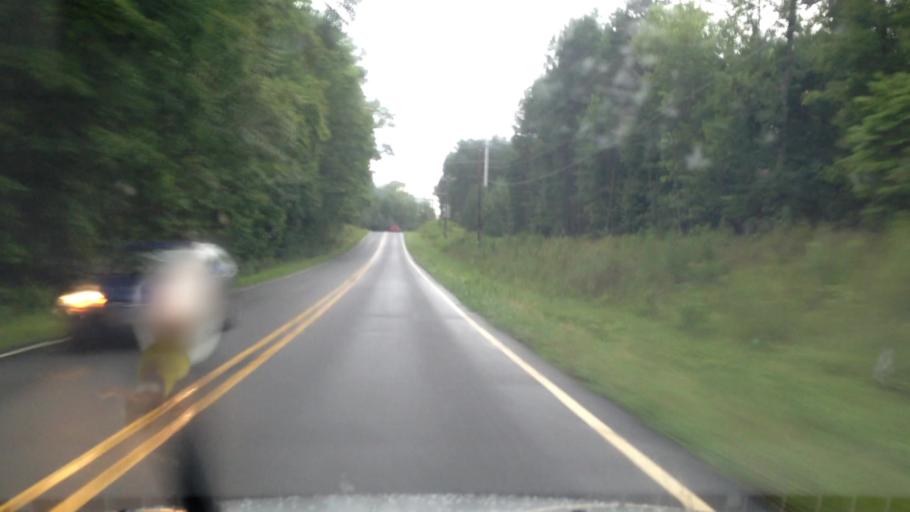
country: US
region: North Carolina
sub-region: Rockingham County
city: Reidsville
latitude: 36.2625
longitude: -79.7256
